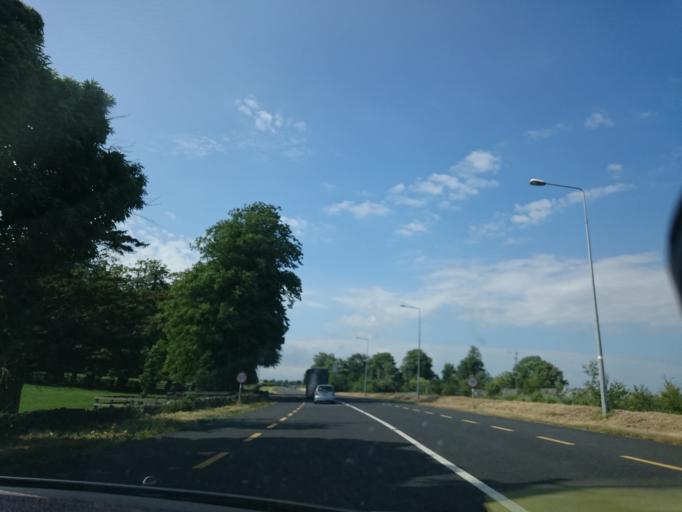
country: IE
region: Leinster
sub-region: Kilkenny
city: Kilkenny
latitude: 52.5751
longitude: -7.2339
